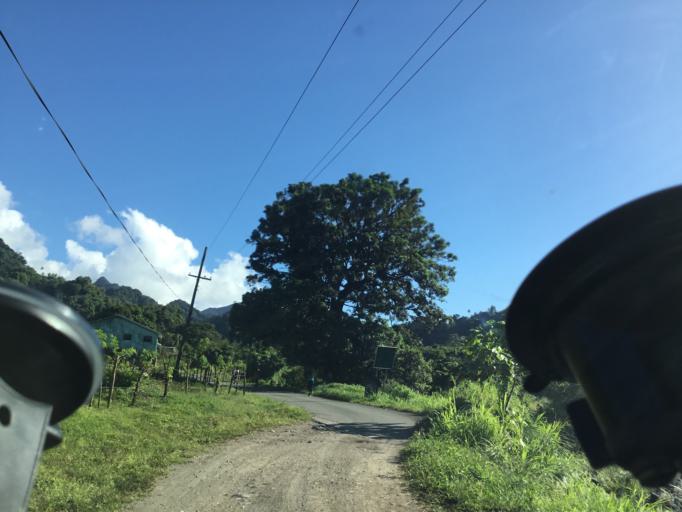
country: VC
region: Saint David
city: Chateaubelair
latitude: 13.3053
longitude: -61.2295
